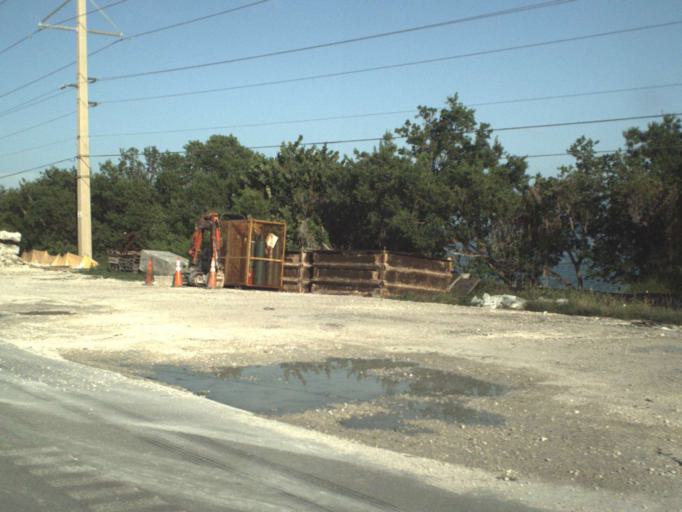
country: US
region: Florida
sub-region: Monroe County
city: Marathon
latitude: 24.7840
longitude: -80.9041
